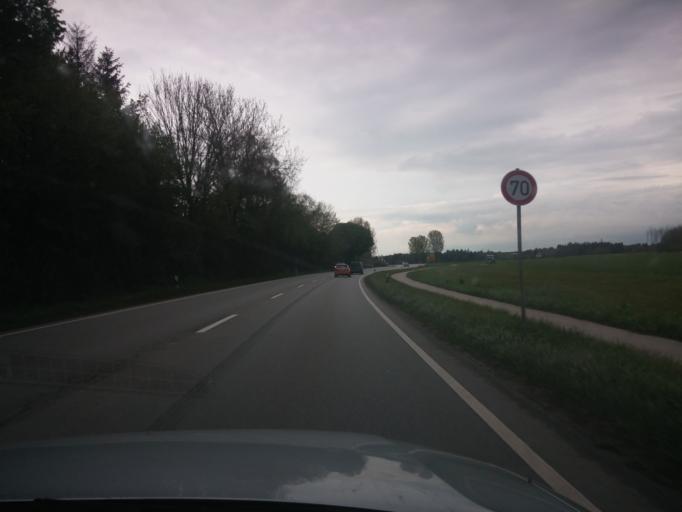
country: DE
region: Bavaria
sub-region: Upper Bavaria
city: Haar
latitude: 48.0932
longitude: 11.7246
